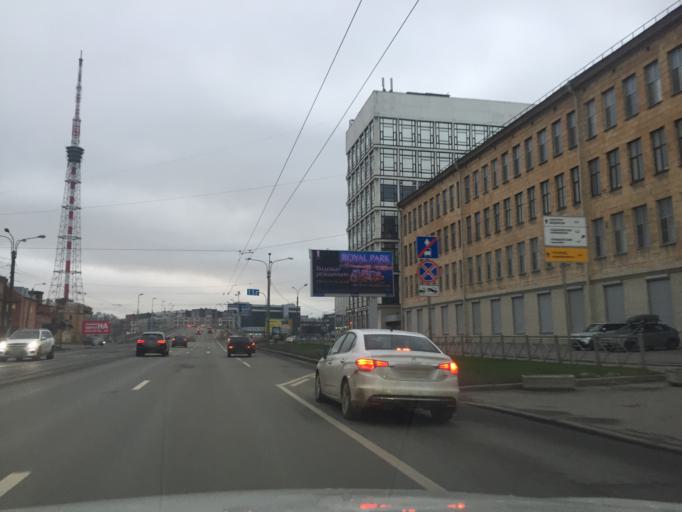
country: RU
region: Leningrad
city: Sampsonievskiy
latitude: 59.9815
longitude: 30.3279
